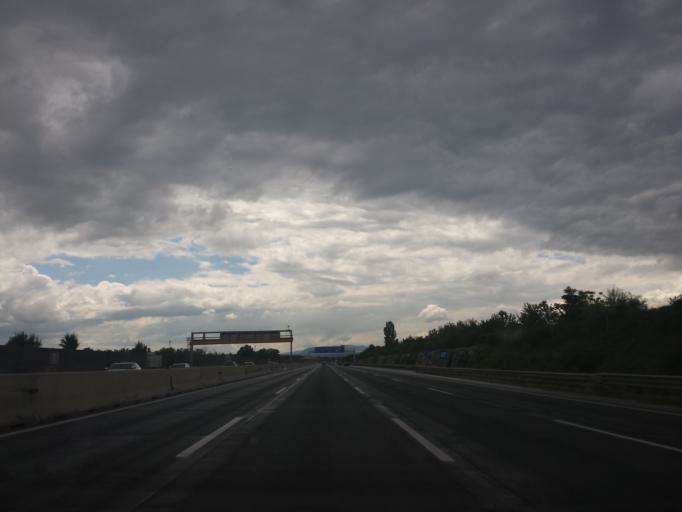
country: AT
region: Lower Austria
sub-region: Politischer Bezirk Baden
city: Traiskirchen
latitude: 47.9969
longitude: 16.2940
